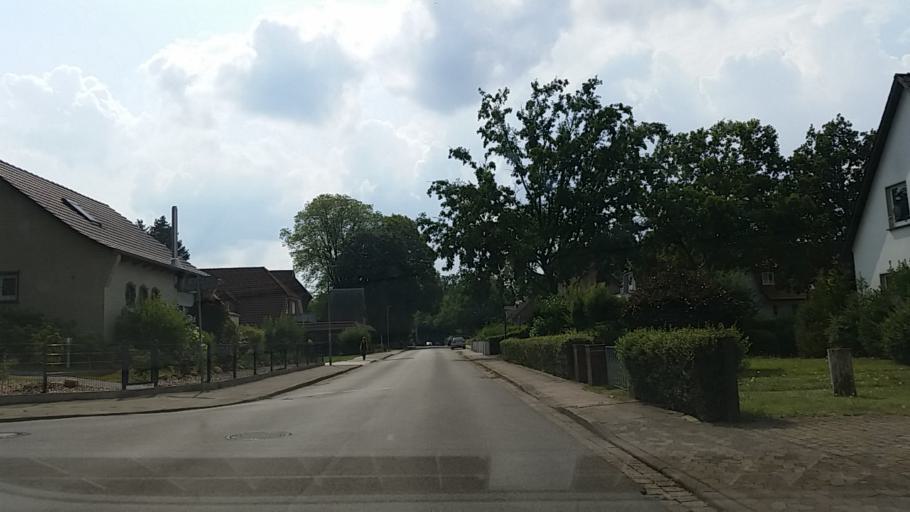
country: DE
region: Lower Saxony
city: Schneverdingen
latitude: 53.1219
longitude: 9.7856
